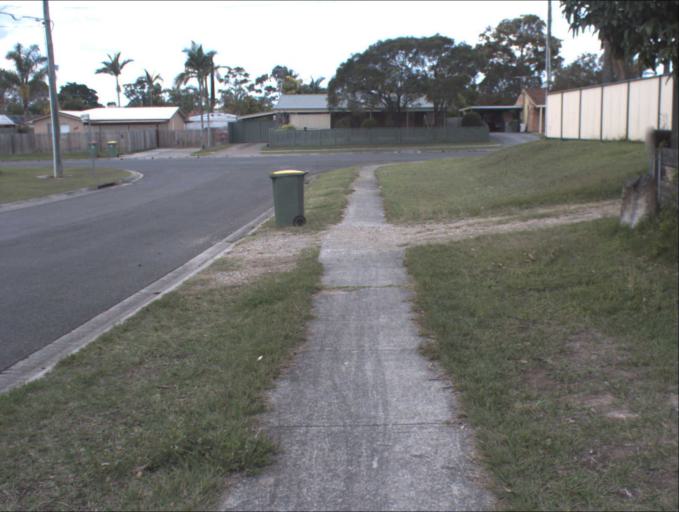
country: AU
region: Queensland
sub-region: Logan
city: Waterford West
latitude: -27.6843
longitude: 153.1505
